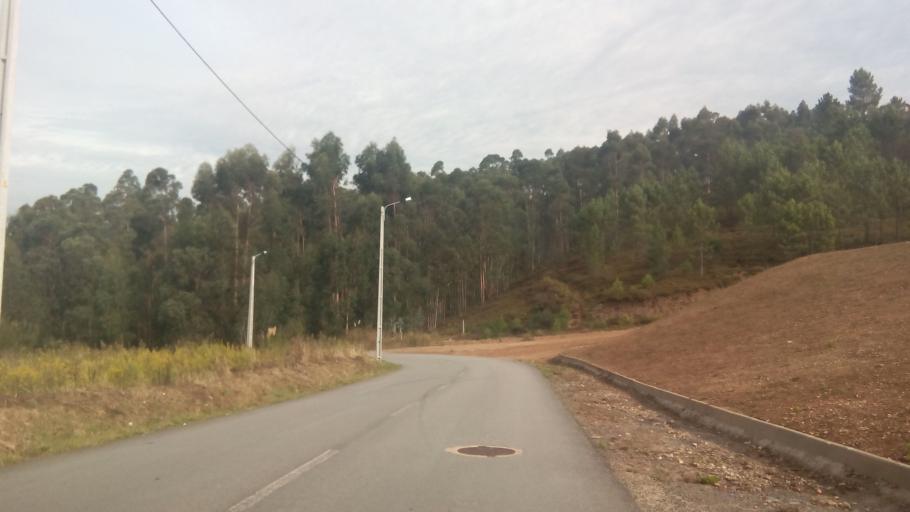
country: PT
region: Porto
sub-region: Paredes
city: Gandra
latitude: 41.1884
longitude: -8.4181
